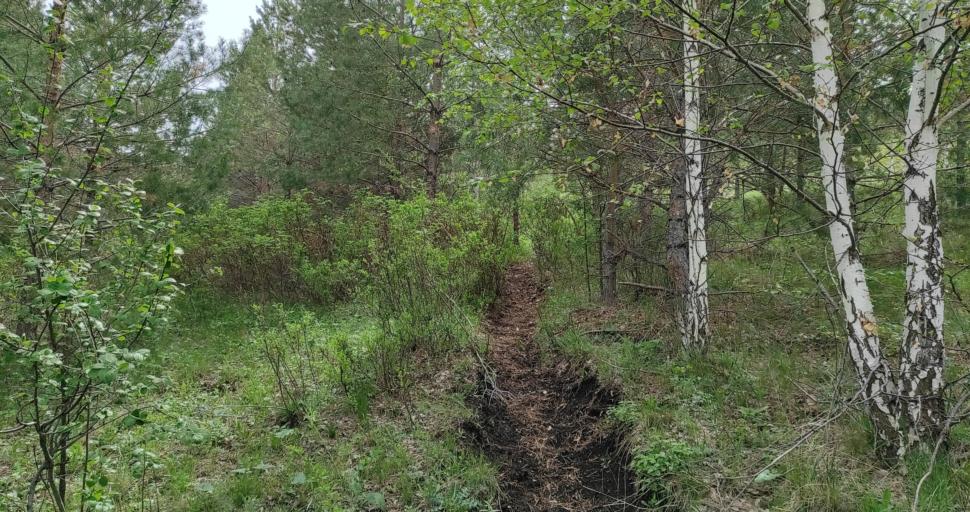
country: RU
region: Bashkortostan
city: Sibay
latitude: 52.6886
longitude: 58.5399
